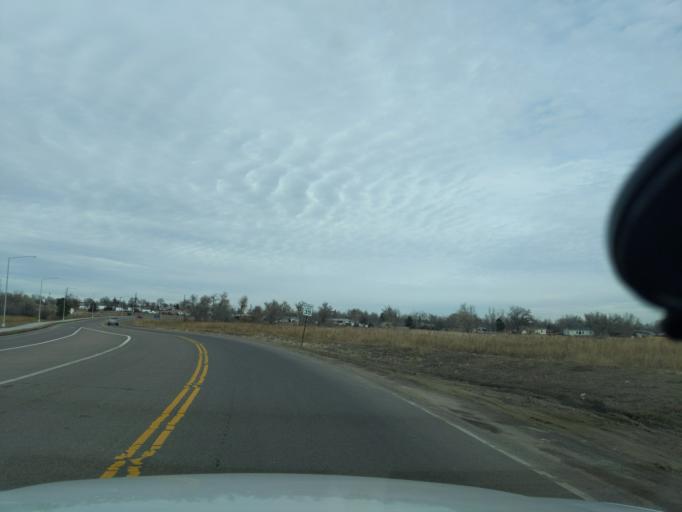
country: US
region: Colorado
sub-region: Adams County
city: Welby
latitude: 39.8565
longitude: -104.9494
